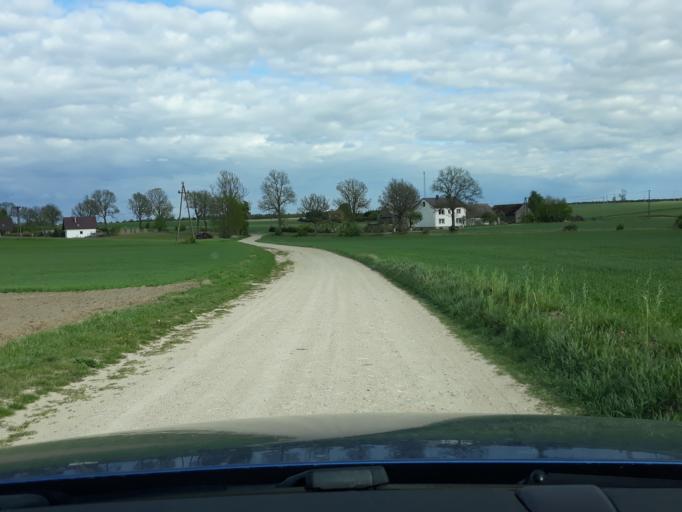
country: PL
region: Pomeranian Voivodeship
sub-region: Powiat czluchowski
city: Czluchow
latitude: 53.7527
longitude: 17.3747
